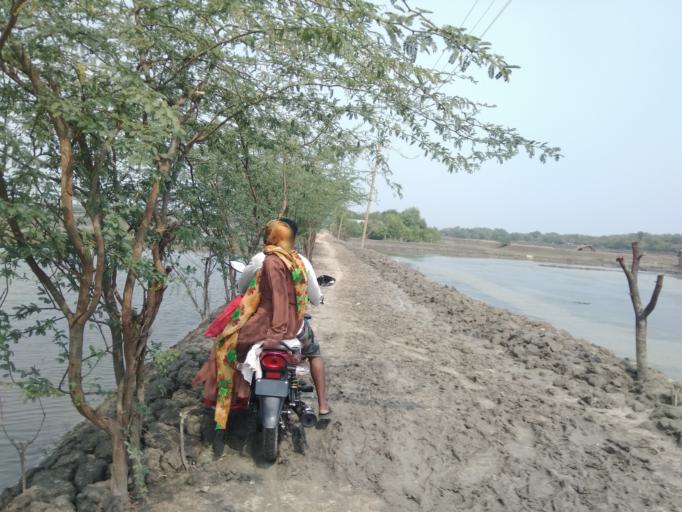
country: IN
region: West Bengal
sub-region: North 24 Parganas
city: Taki
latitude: 22.2764
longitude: 89.2843
